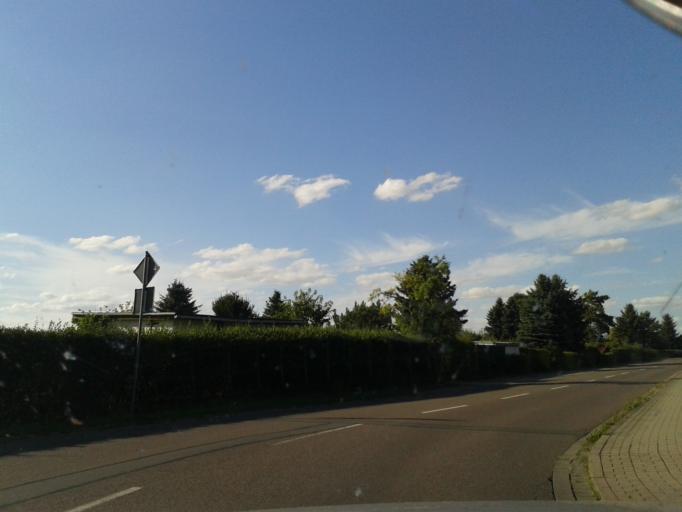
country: DE
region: Saxony-Anhalt
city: Braschwitz
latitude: 51.5216
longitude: 12.0568
